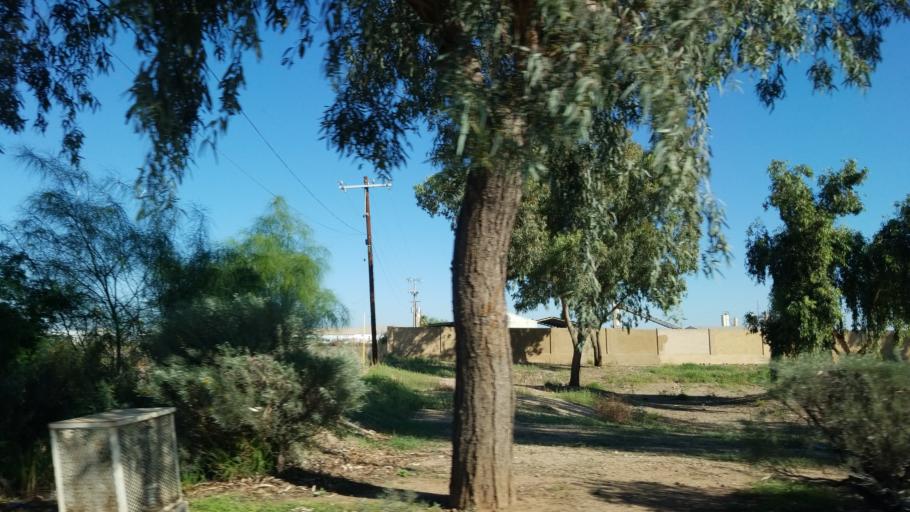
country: US
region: Arizona
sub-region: Maricopa County
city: Glendale
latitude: 33.5241
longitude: -112.1760
